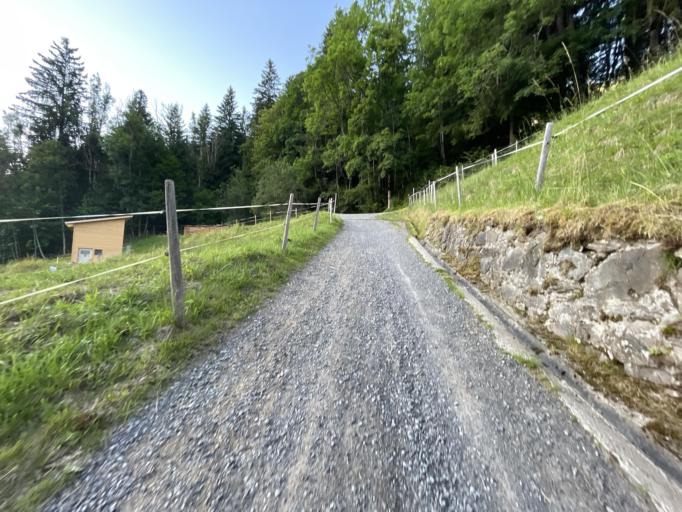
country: CH
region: Bern
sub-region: Interlaken-Oberhasli District
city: Lauterbrunnen
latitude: 46.6005
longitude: 7.9187
